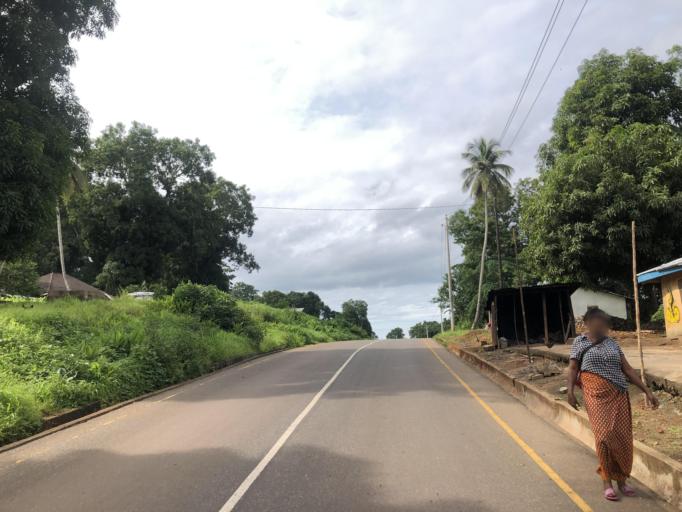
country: SL
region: Northern Province
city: Port Loko
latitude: 8.7559
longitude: -12.7874
